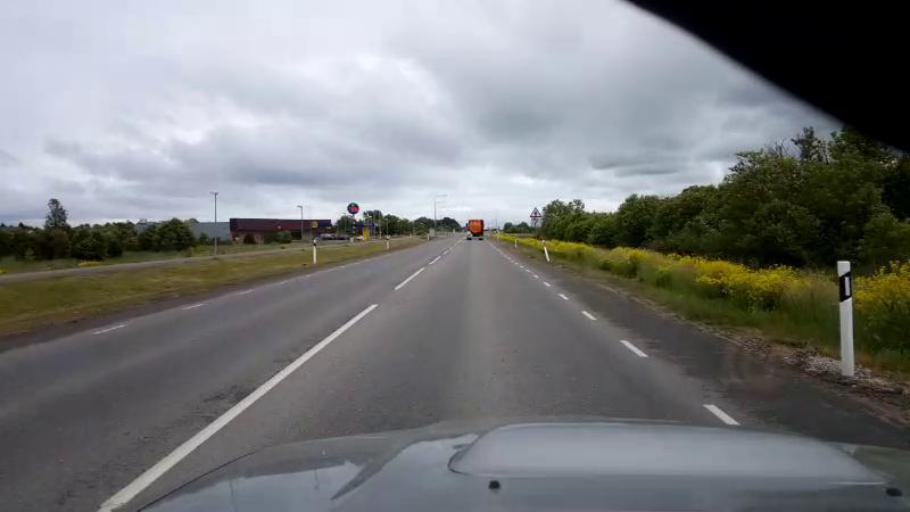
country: EE
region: Harju
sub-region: Harku vald
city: Tabasalu
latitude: 59.4545
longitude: 24.4401
